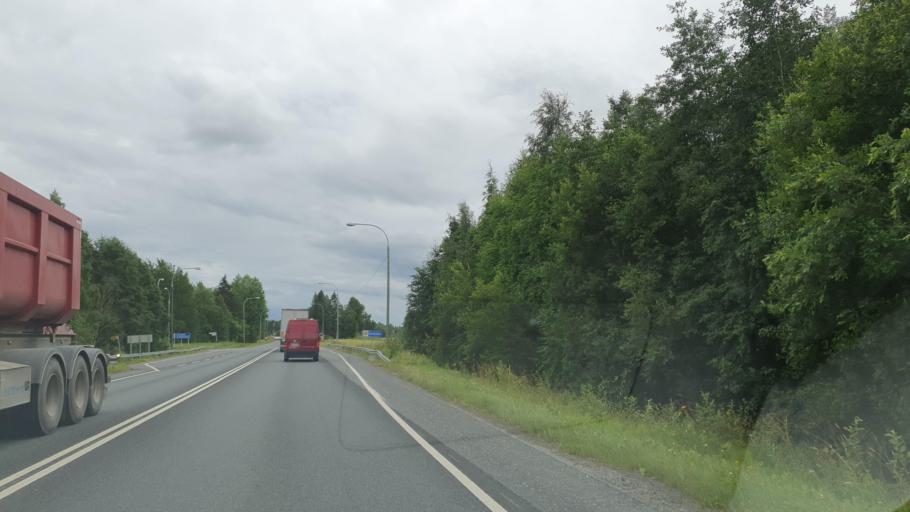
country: FI
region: Northern Savo
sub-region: Ylae-Savo
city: Lapinlahti
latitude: 63.4579
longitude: 27.3145
